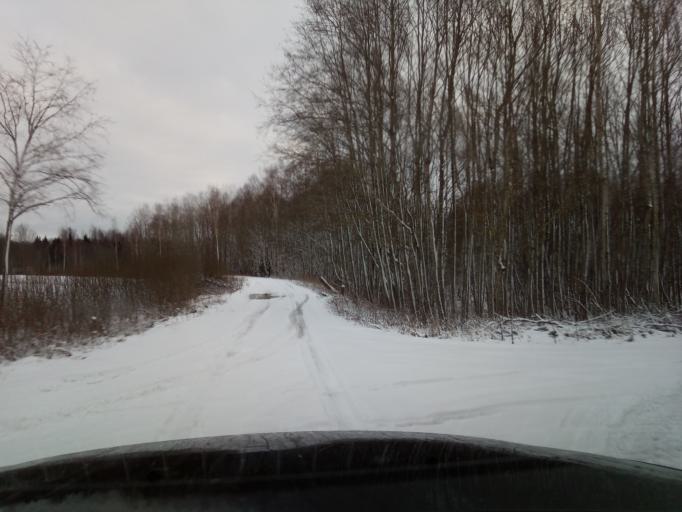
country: LT
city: Zarasai
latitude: 55.7328
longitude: 25.9420
